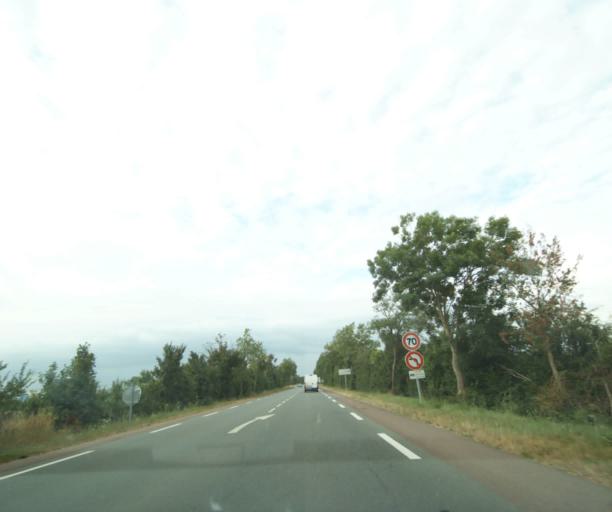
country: FR
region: Poitou-Charentes
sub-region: Departement de la Charente-Maritime
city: Marans
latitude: 46.2816
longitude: -0.9957
